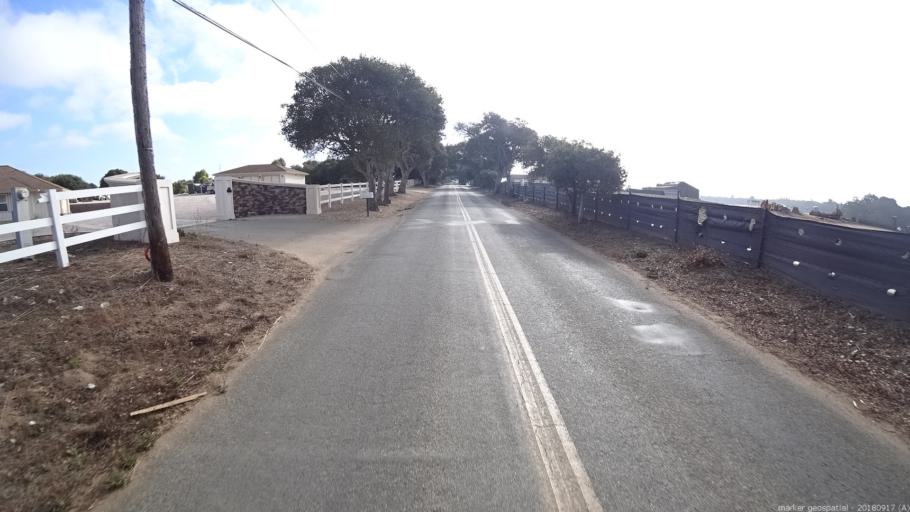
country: US
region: California
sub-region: Monterey County
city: Elkhorn
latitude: 36.7895
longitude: -121.7167
